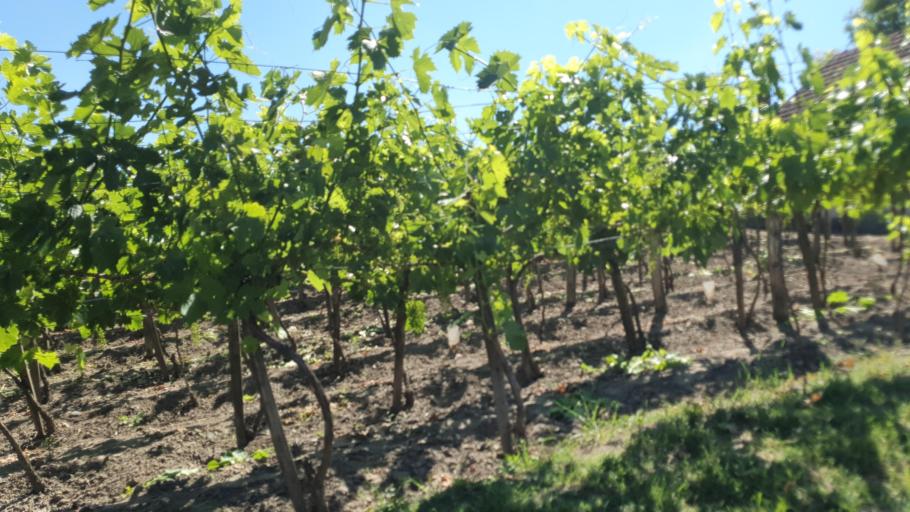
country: HU
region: Bacs-Kiskun
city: Hajos
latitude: 46.3868
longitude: 19.1530
